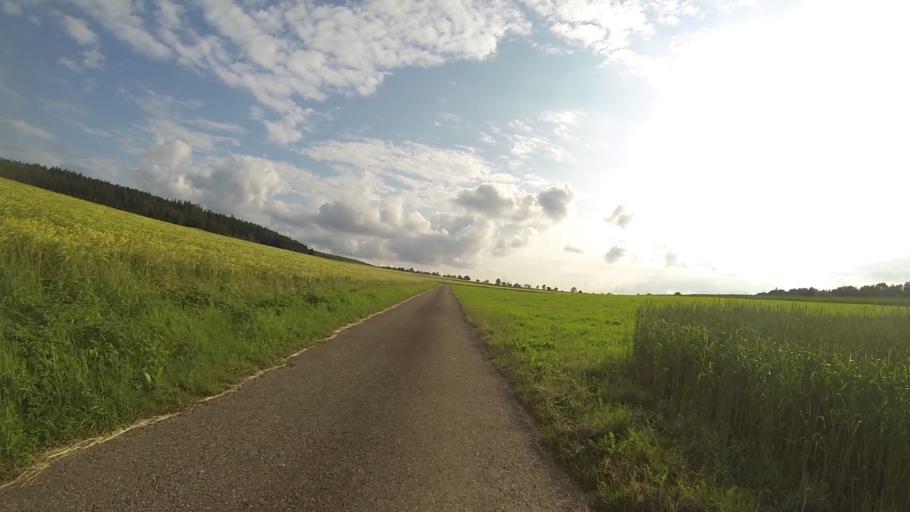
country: DE
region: Baden-Wuerttemberg
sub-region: Regierungsbezirk Stuttgart
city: Neresheim
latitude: 48.7377
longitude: 10.2822
